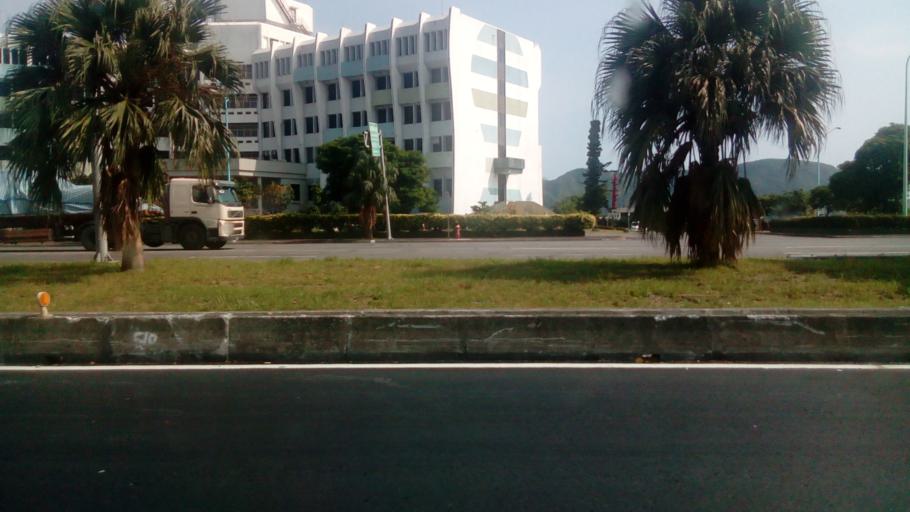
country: TW
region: Taiwan
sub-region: Yilan
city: Yilan
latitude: 24.5963
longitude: 121.8560
